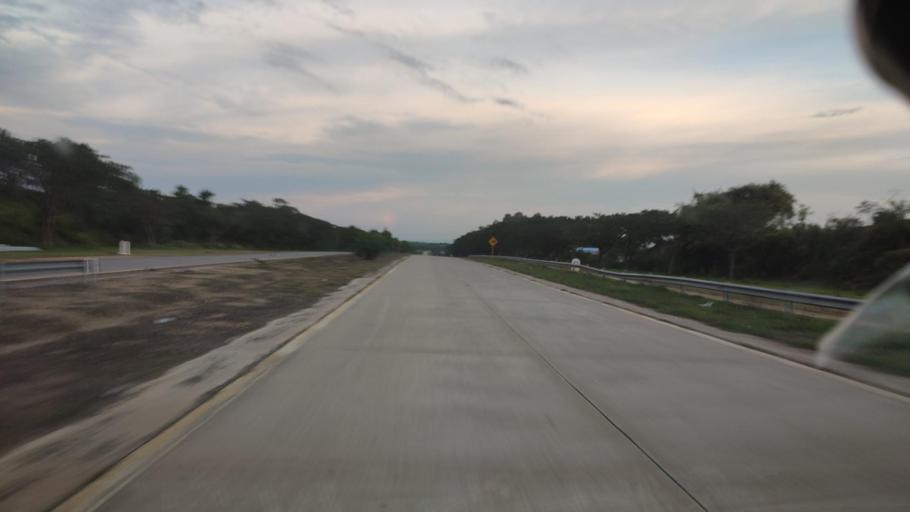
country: MM
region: Mandalay
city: Yamethin
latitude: 20.3026
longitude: 95.8824
